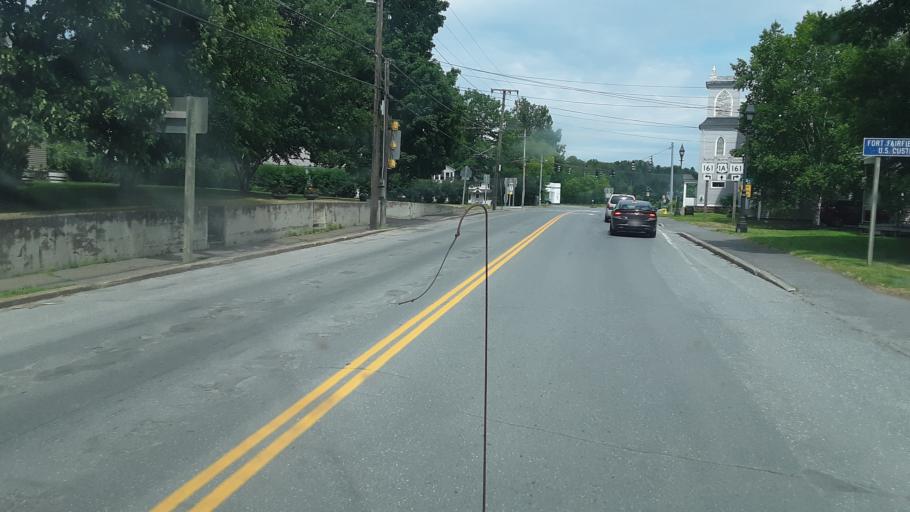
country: US
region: Maine
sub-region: Aroostook County
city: Fort Fairfield
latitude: 46.7720
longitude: -67.8369
